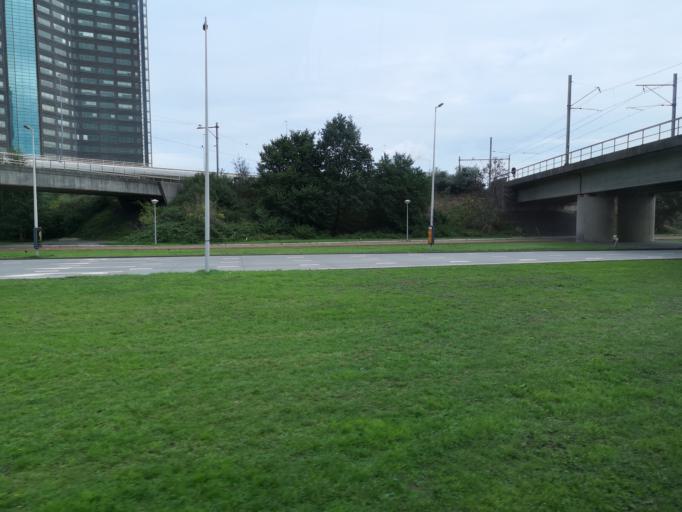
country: NL
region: North Holland
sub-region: Gemeente Zaanstad
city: Zaandam
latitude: 52.3918
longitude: 4.8377
